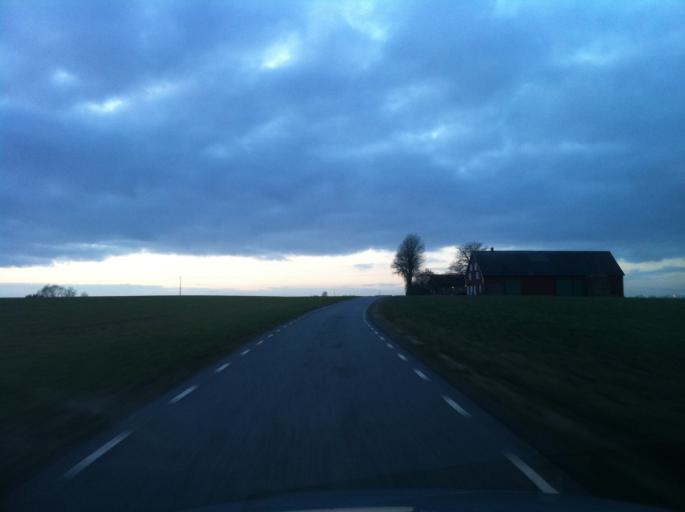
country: SE
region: Skane
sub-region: Svalovs Kommun
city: Teckomatorp
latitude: 55.8617
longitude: 13.0436
